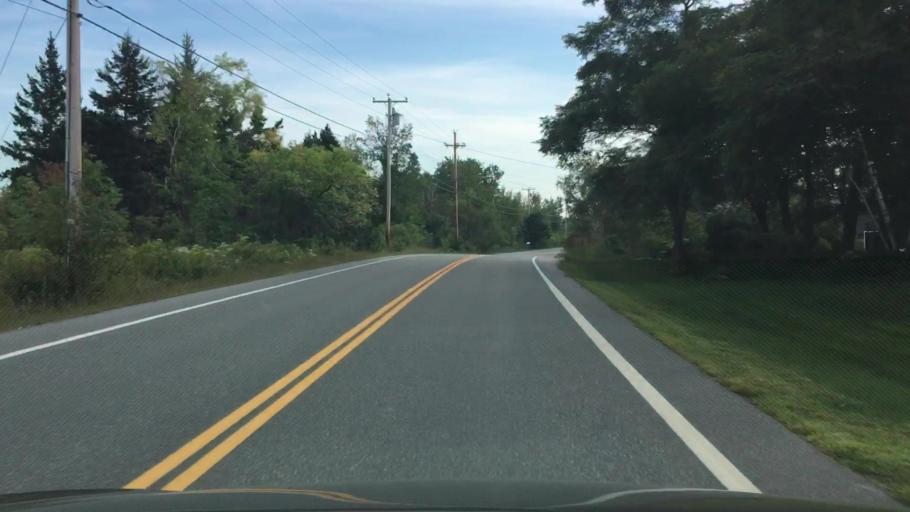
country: US
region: Maine
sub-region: Hancock County
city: Castine
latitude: 44.4431
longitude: -68.7872
